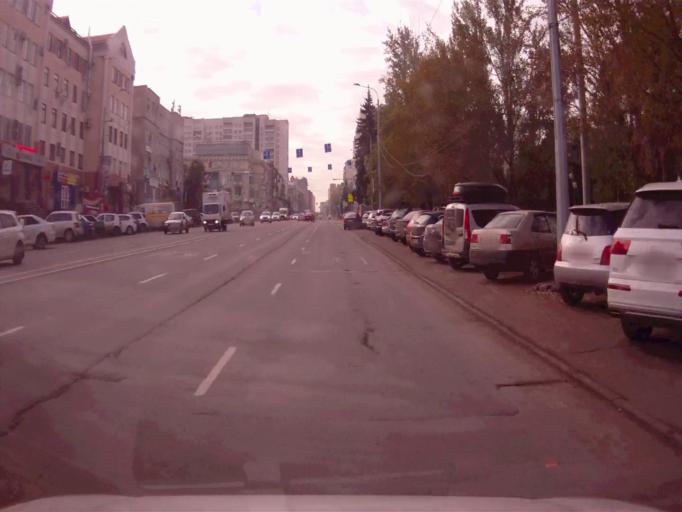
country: RU
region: Chelyabinsk
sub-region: Gorod Chelyabinsk
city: Chelyabinsk
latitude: 55.1615
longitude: 61.3935
